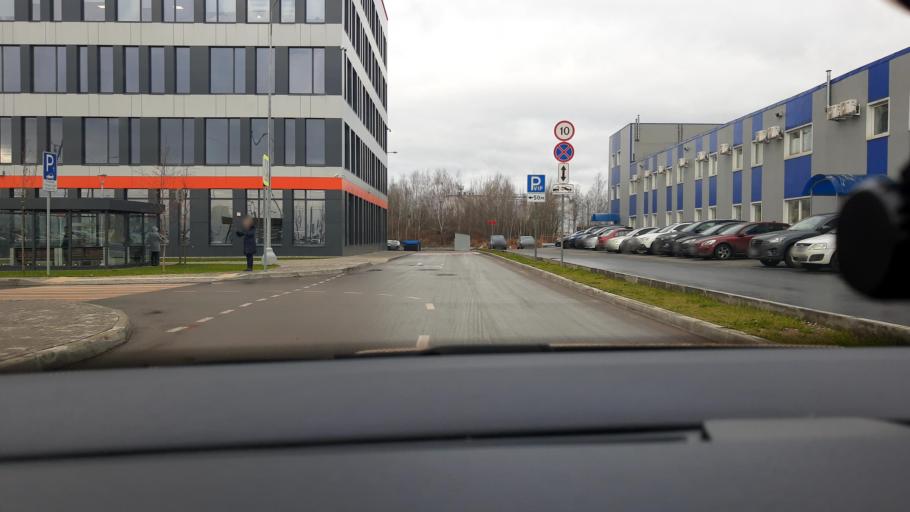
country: RU
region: Moskovskaya
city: Lobnya
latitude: 55.9851
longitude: 37.4290
